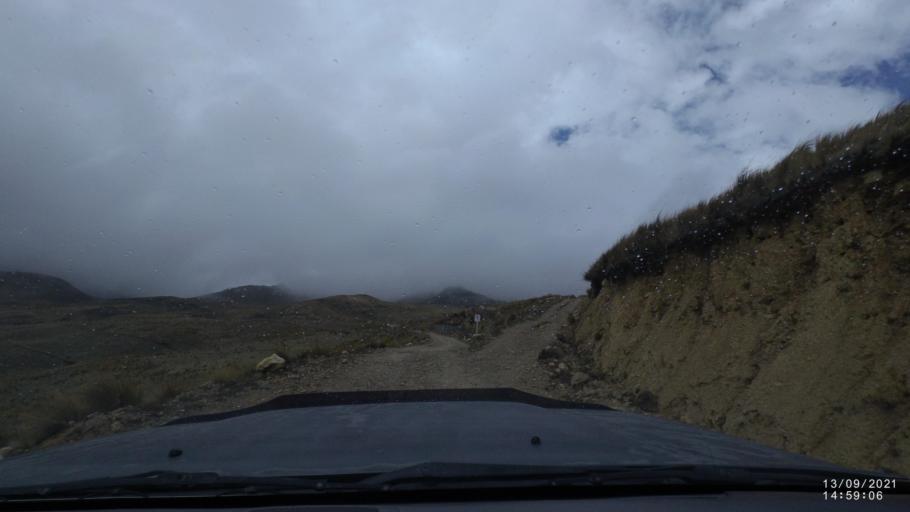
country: BO
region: Cochabamba
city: Colomi
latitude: -17.3316
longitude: -65.7883
